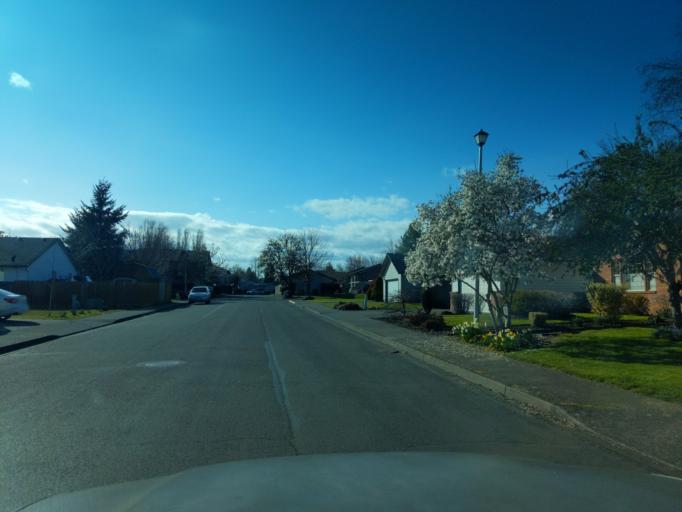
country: US
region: Oregon
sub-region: Yamhill County
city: McMinnville
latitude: 45.2027
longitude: -123.2161
